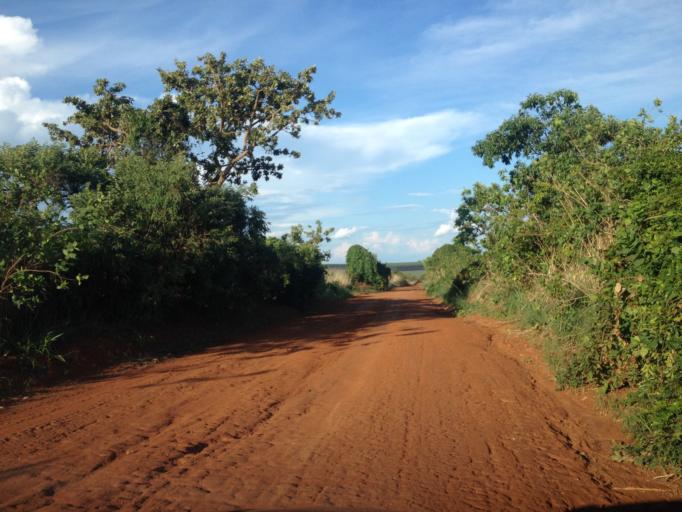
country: BR
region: Goias
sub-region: Abadiania
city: Abadiania
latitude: -16.0049
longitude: -48.5574
